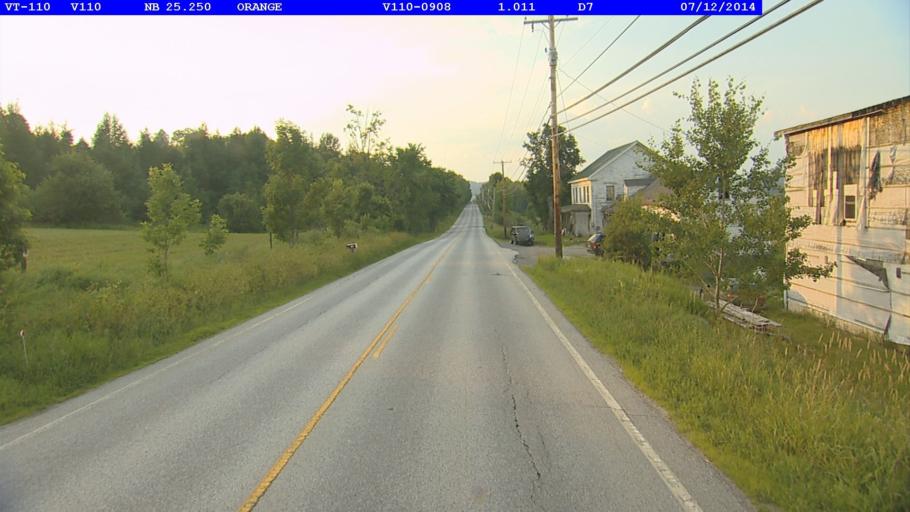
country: US
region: Vermont
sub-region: Washington County
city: South Barre
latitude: 44.1386
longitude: -72.4328
